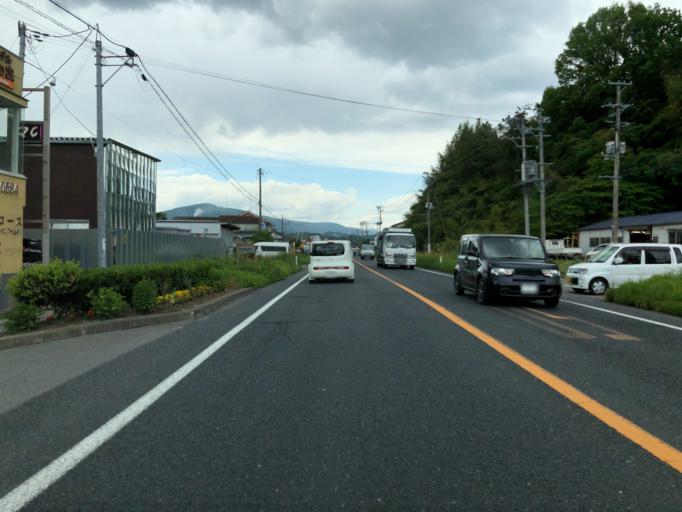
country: JP
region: Fukushima
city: Iwaki
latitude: 36.9905
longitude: 140.8661
